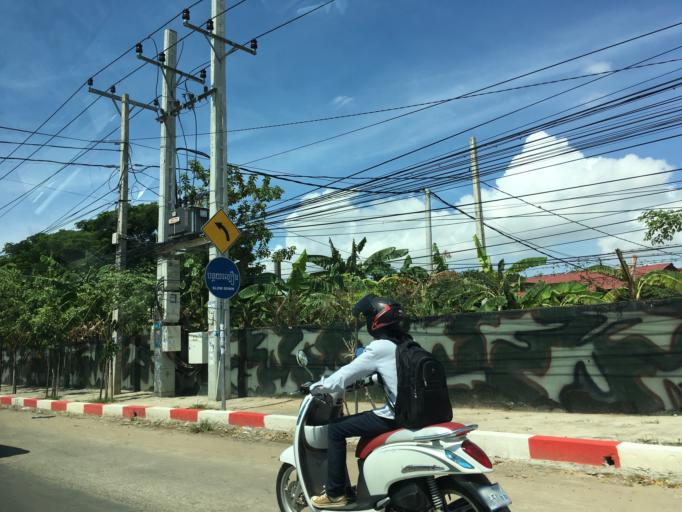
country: KH
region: Phnom Penh
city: Phnom Penh
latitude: 11.5512
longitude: 104.8578
